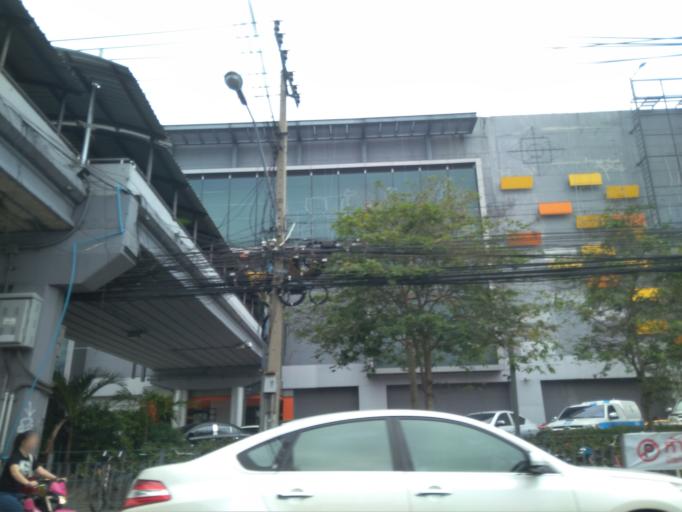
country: TH
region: Bangkok
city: Bang Na
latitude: 13.6930
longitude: 100.6473
